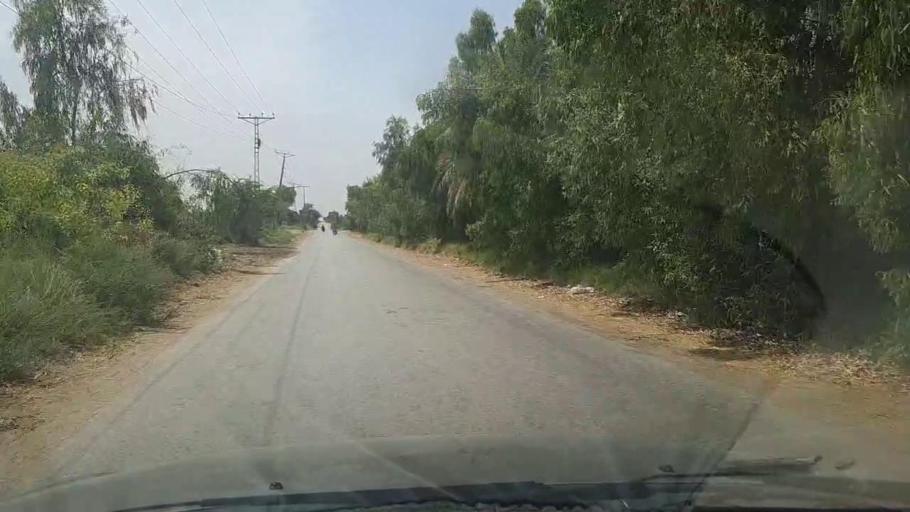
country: PK
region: Sindh
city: Bhiria
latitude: 26.9033
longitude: 68.2058
